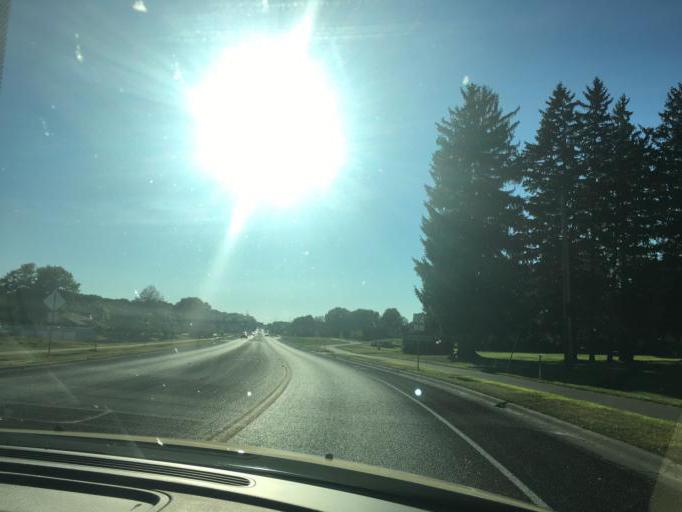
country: US
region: Minnesota
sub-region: Olmsted County
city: Rochester
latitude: 44.0795
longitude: -92.5246
